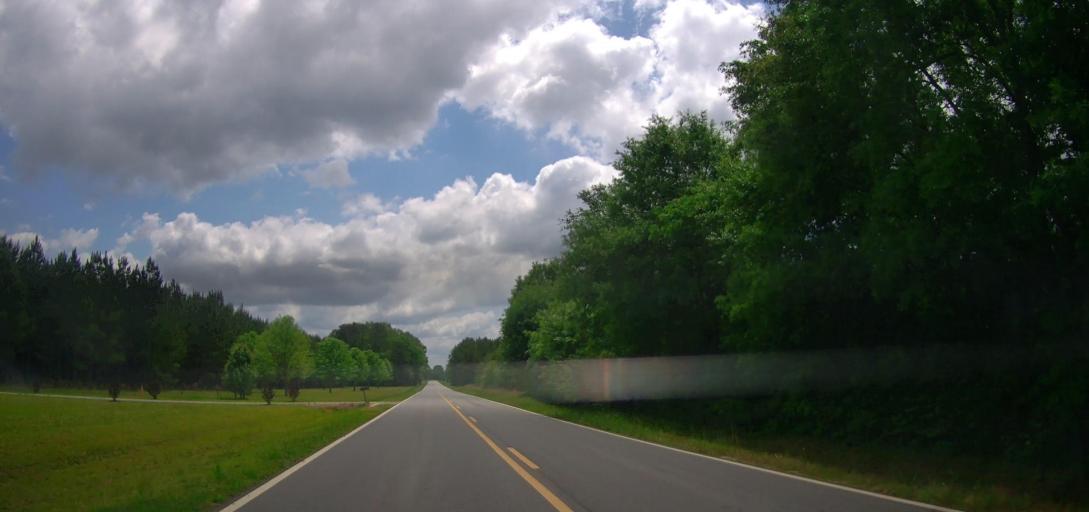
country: US
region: Georgia
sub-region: Laurens County
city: Dublin
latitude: 32.5974
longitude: -82.9540
